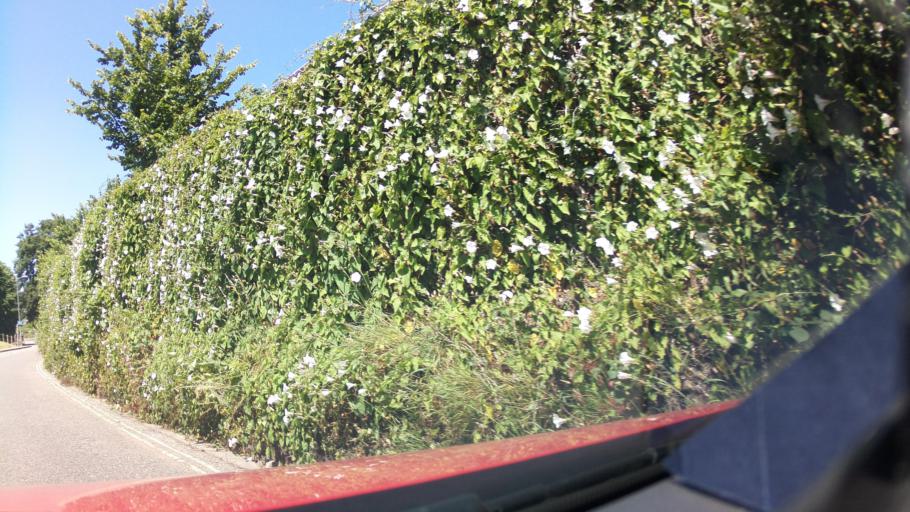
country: GB
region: England
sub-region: Borough of Torbay
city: Torquay
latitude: 50.4614
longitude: -3.5428
